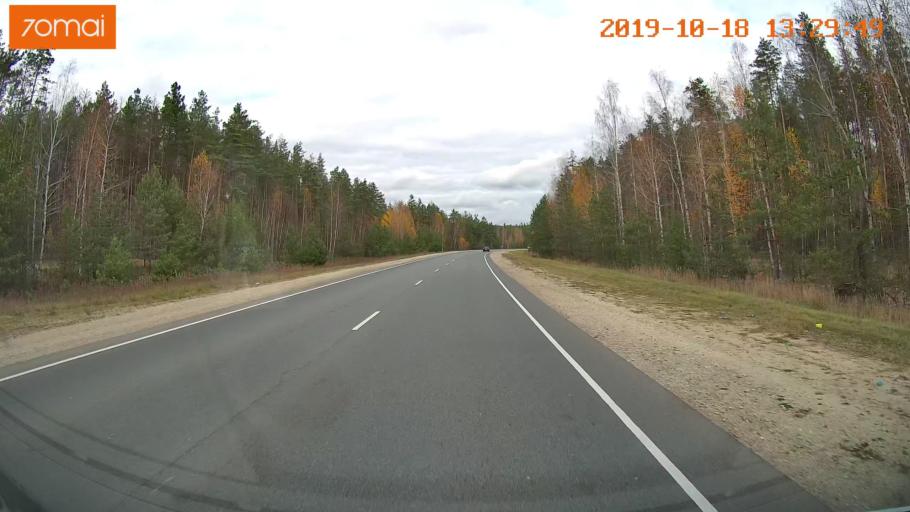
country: RU
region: Rjazan
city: Solotcha
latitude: 54.8009
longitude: 39.8776
